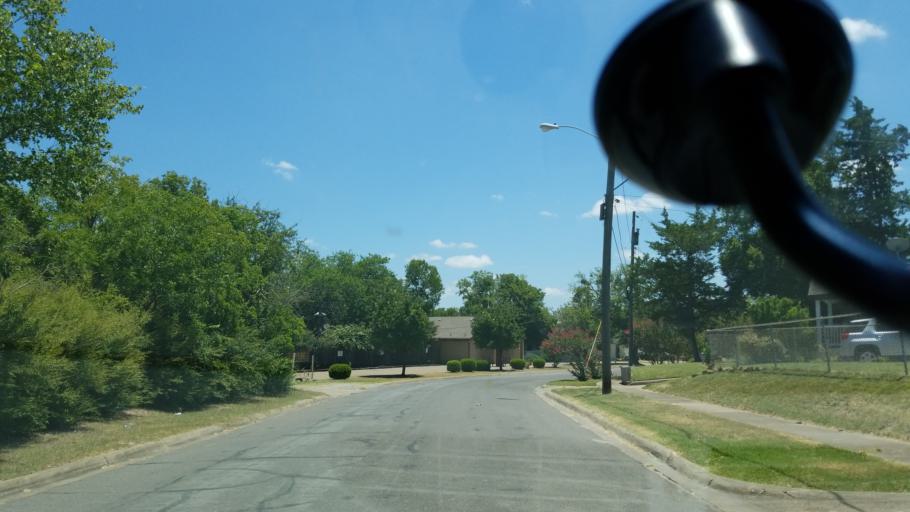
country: US
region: Texas
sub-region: Dallas County
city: Cockrell Hill
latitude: 32.6980
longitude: -96.8121
